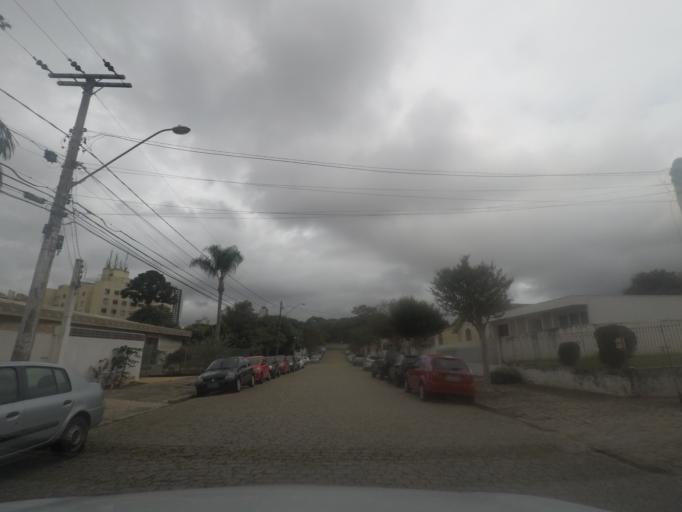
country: BR
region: Parana
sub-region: Curitiba
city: Curitiba
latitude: -25.4406
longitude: -49.2418
